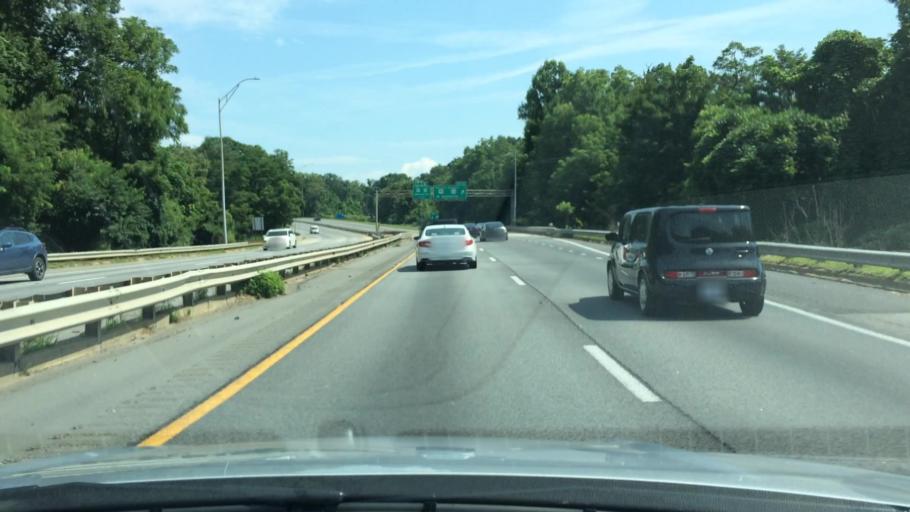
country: US
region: North Carolina
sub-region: Buncombe County
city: Asheville
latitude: 35.5725
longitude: -82.5843
